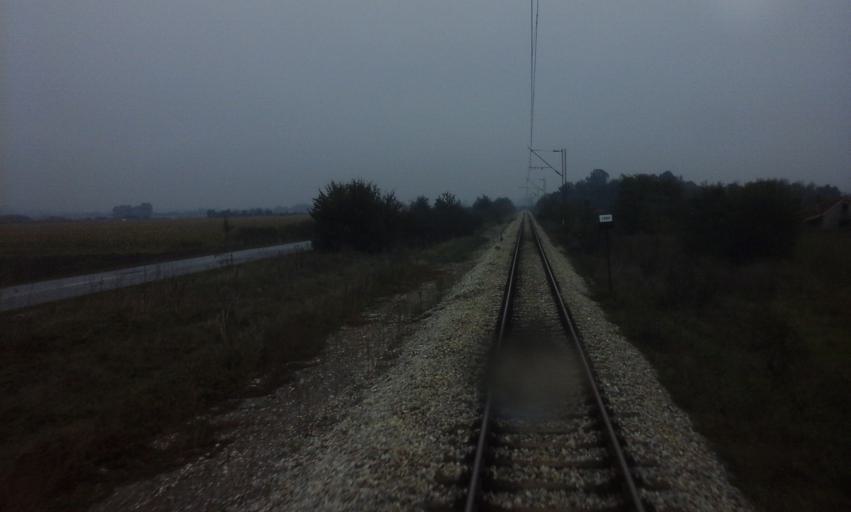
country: RS
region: Central Serbia
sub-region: Pomoravski Okrug
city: Cuprija
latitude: 43.8921
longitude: 21.3818
